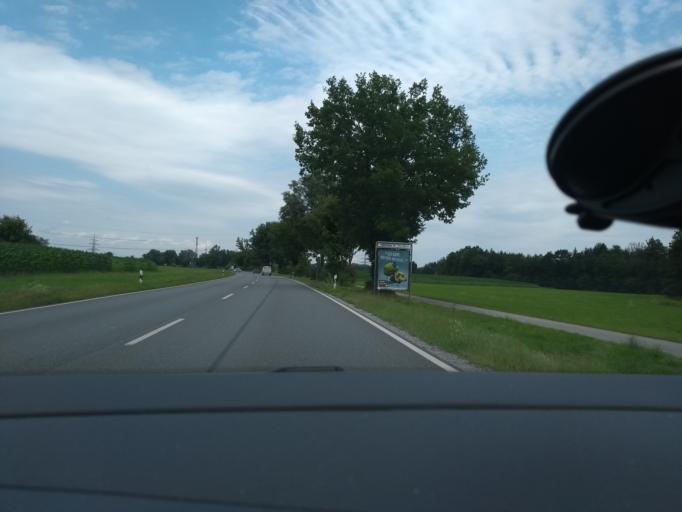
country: DE
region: Bavaria
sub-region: Upper Bavaria
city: Schechen
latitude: 47.9056
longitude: 12.1261
